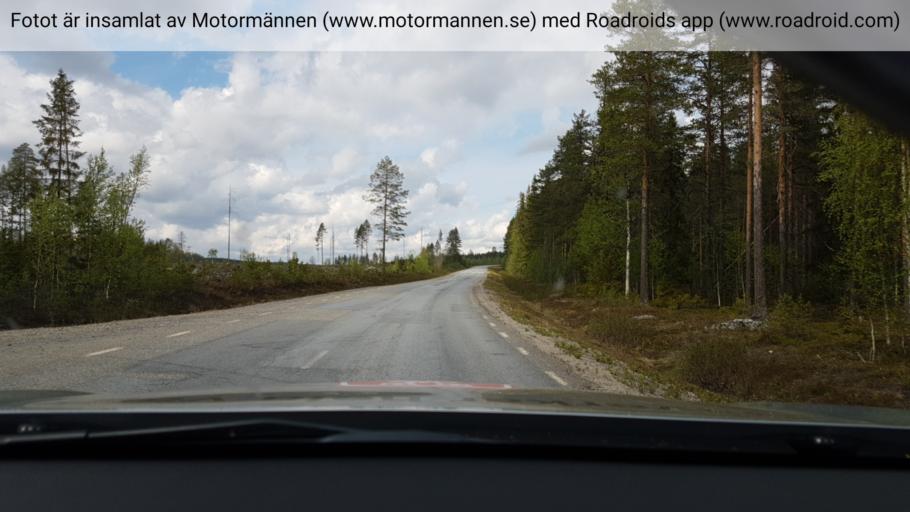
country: SE
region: Vaesternorrland
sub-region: OErnskoeldsviks Kommun
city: Bredbyn
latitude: 63.8931
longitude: 18.5096
